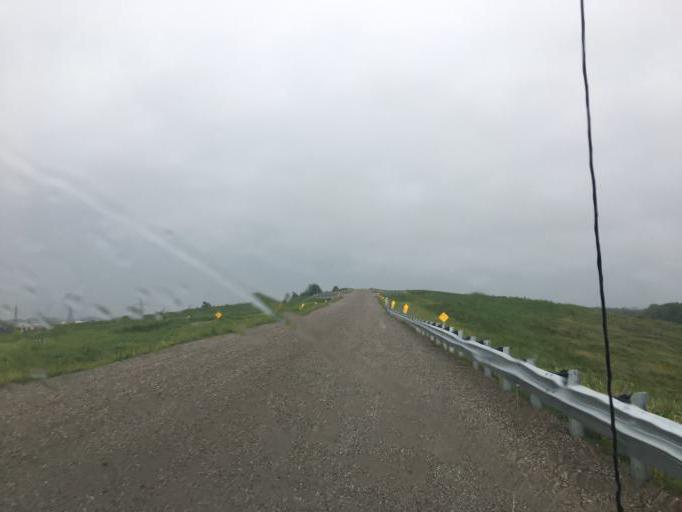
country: CA
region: Ontario
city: Waterloo
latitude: 43.4407
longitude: -80.5759
